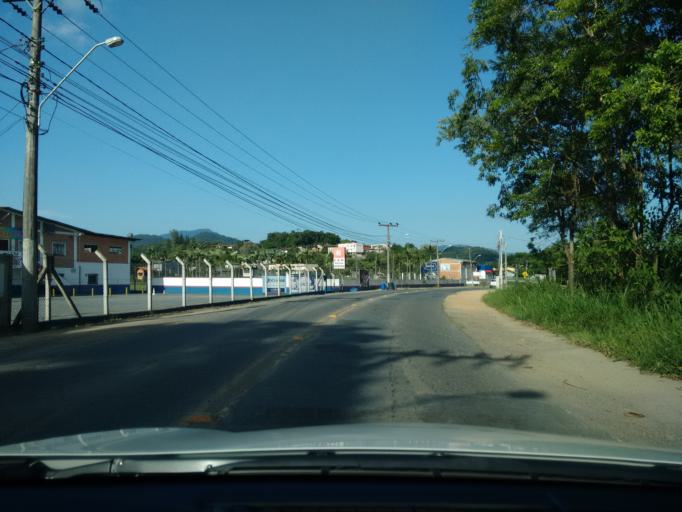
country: BR
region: Santa Catarina
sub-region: Blumenau
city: Blumenau
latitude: -26.8504
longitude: -49.0864
